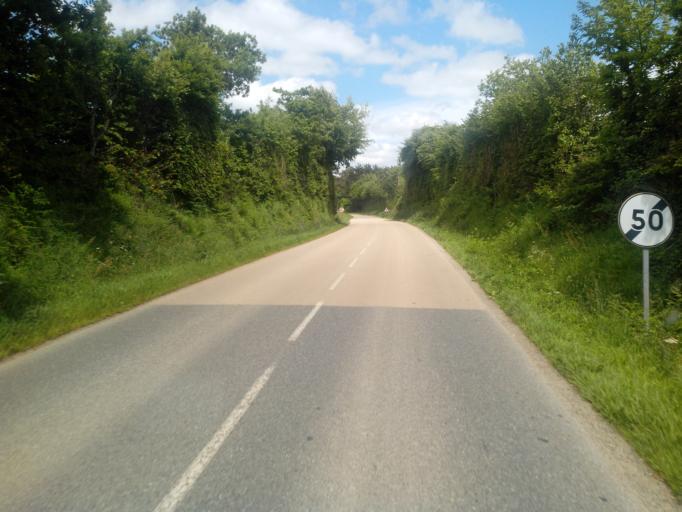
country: FR
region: Brittany
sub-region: Departement du Finistere
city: Guerlesquin
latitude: 48.5015
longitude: -3.6118
